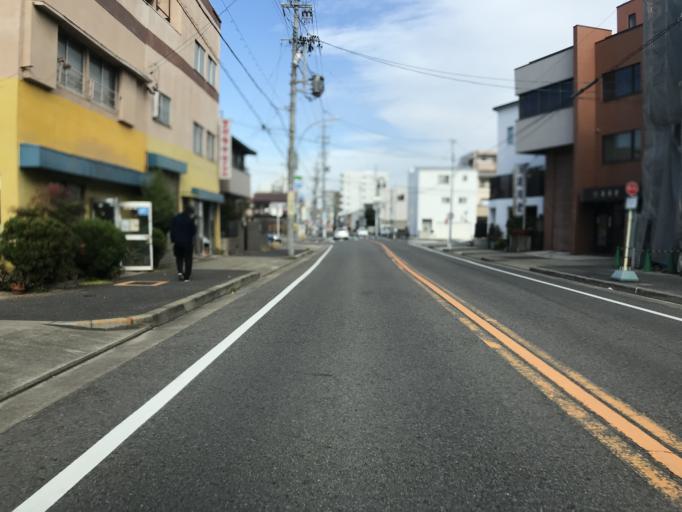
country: JP
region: Aichi
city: Nagoya-shi
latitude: 35.1886
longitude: 136.9243
